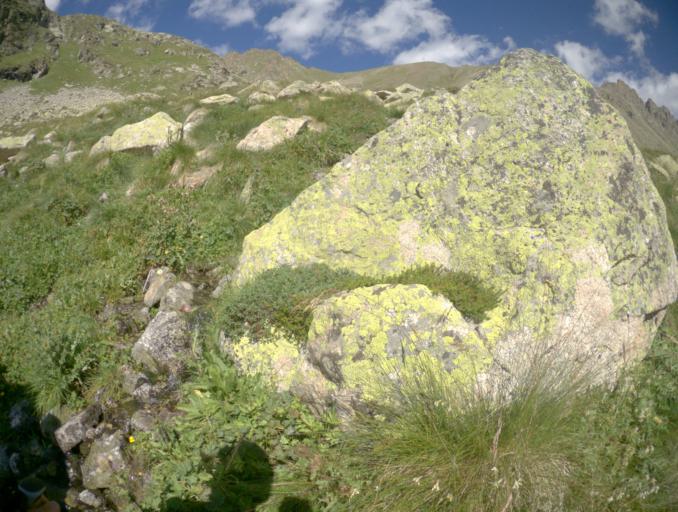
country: RU
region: Karachayevo-Cherkesiya
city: Uchkulan
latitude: 43.3250
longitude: 42.0993
